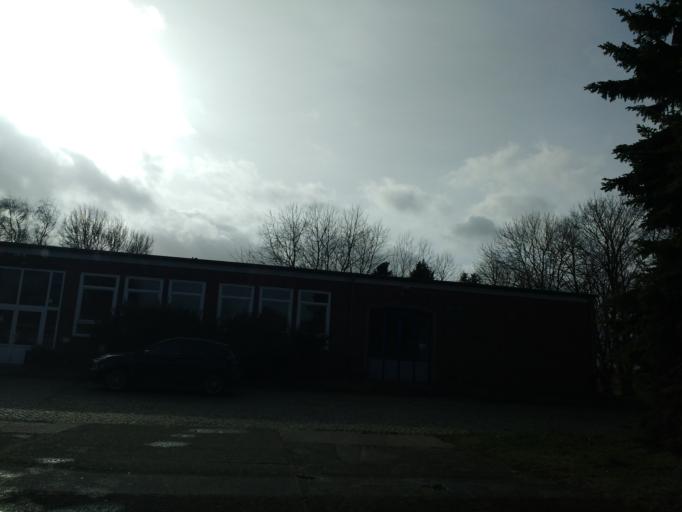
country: DE
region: Schleswig-Holstein
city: Heiligenhafen
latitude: 54.3757
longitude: 10.9531
